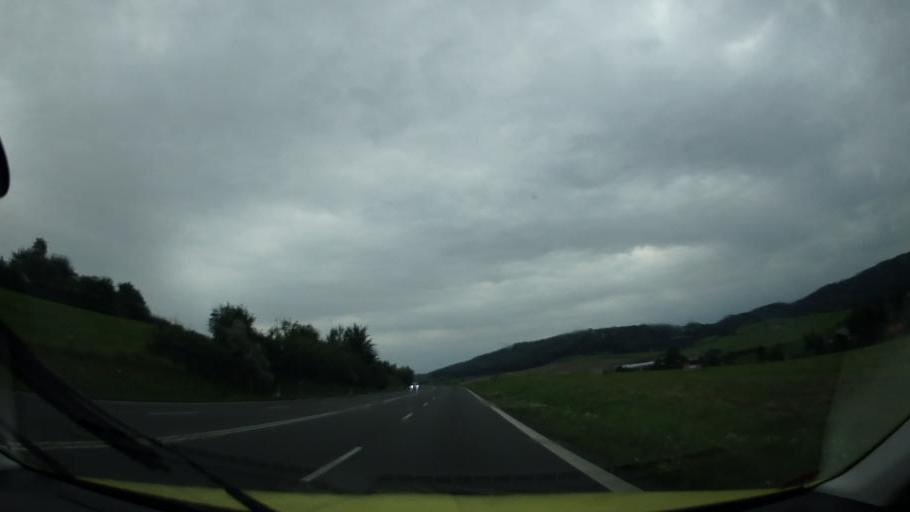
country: CZ
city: Vlcnov
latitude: 49.5709
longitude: 17.9514
